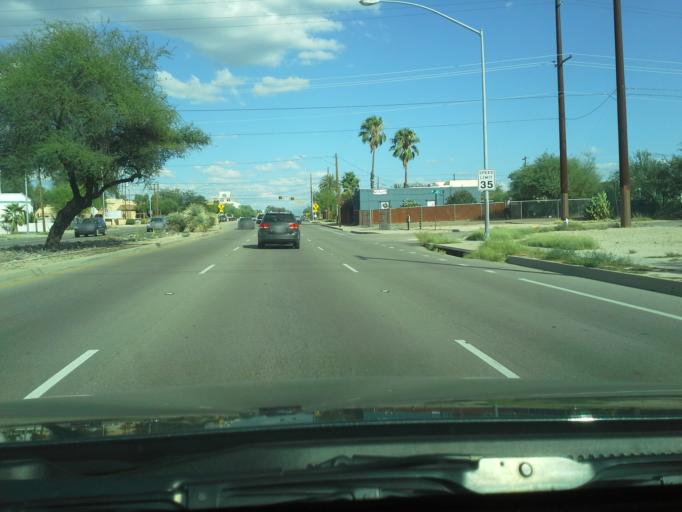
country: US
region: Arizona
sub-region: Pima County
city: South Tucson
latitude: 32.2358
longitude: -110.9769
